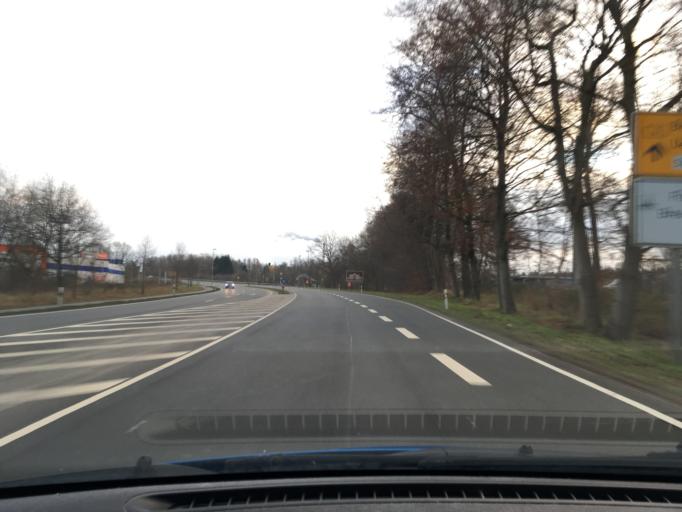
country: DE
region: Lower Saxony
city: Uelzen
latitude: 52.9892
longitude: 10.5458
